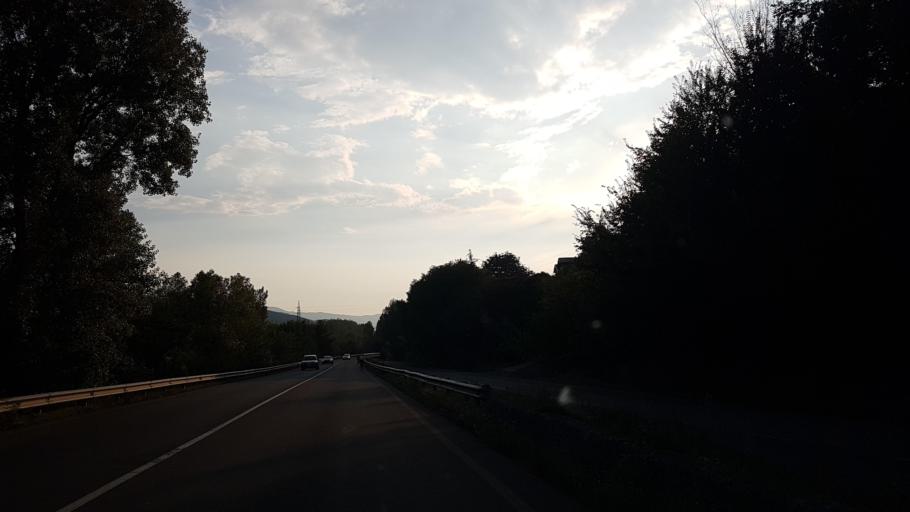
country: IT
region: Emilia-Romagna
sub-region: Provincia di Parma
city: Borgo Val di Taro
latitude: 44.4984
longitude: 9.8008
